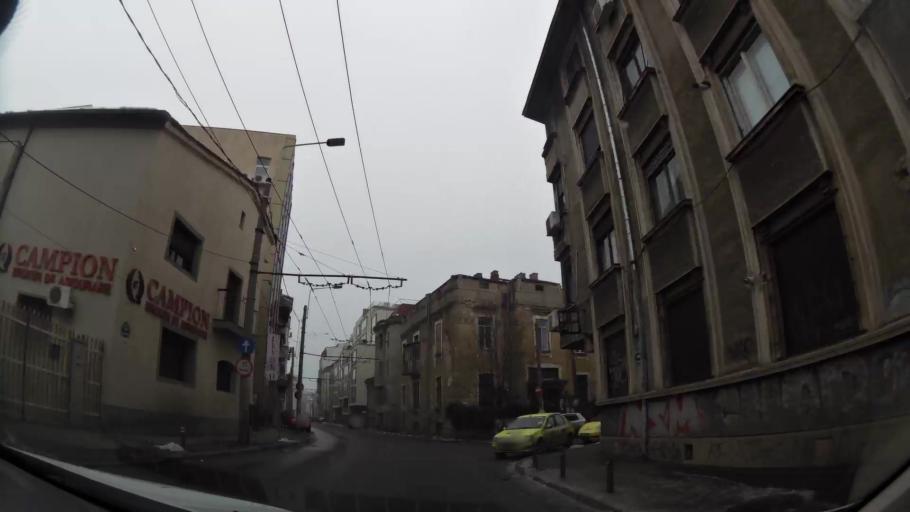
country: RO
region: Bucuresti
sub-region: Municipiul Bucuresti
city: Bucuresti
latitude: 44.4474
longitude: 26.0851
